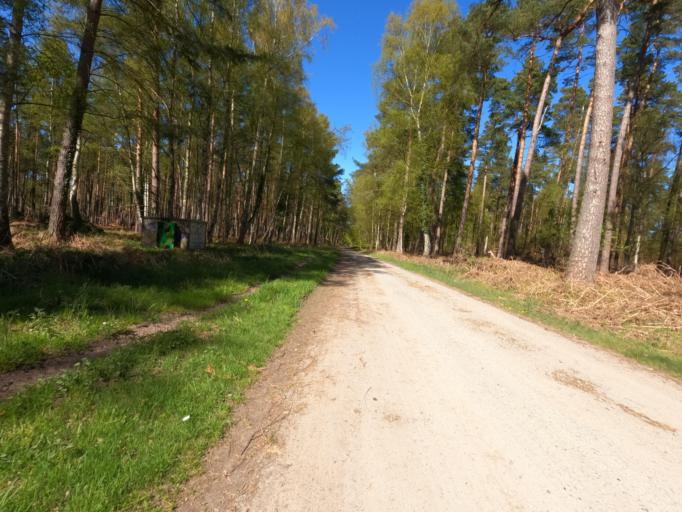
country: DE
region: Mecklenburg-Vorpommern
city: Born
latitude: 54.4137
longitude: 12.5320
